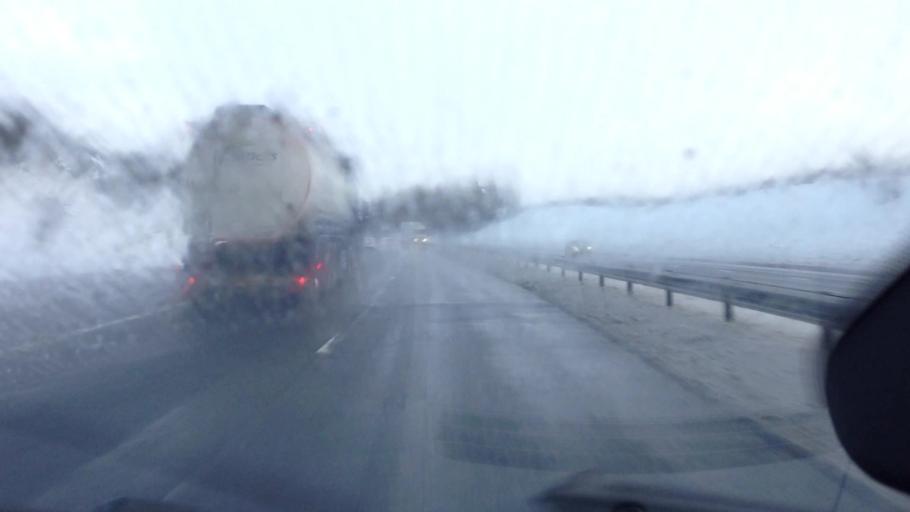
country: GB
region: Scotland
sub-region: South Lanarkshire
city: Blackwood
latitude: 55.6614
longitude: -3.9205
